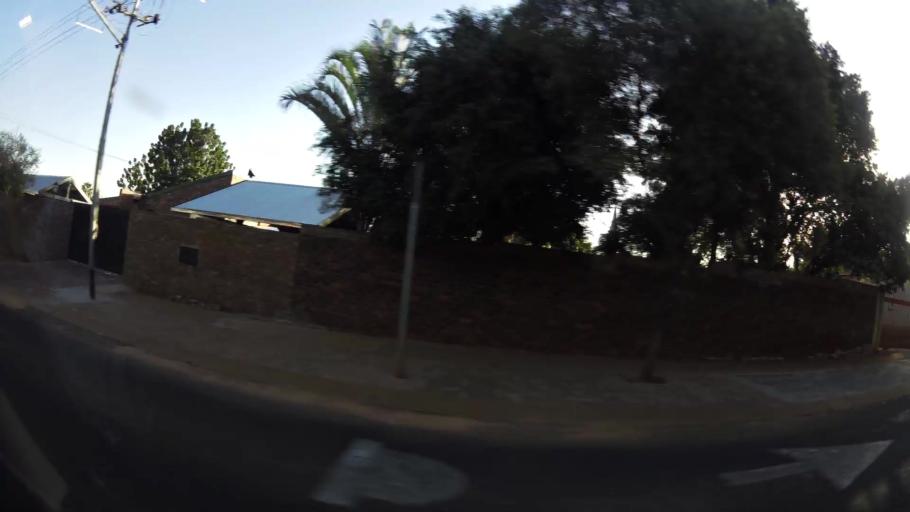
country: ZA
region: Gauteng
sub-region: City of Tshwane Metropolitan Municipality
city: Pretoria
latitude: -25.7002
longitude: 28.2089
